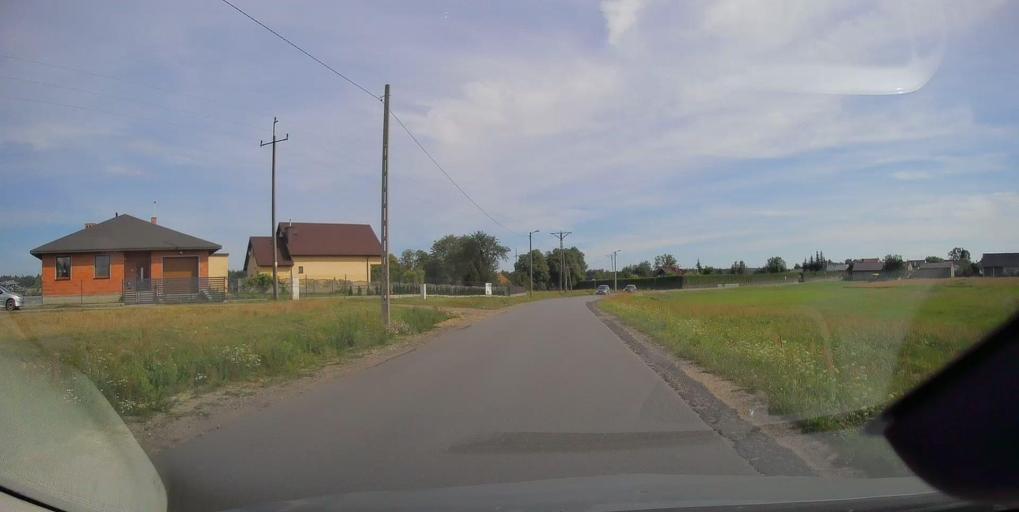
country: PL
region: Lodz Voivodeship
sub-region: Powiat tomaszowski
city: Tomaszow Mazowiecki
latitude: 51.4577
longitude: 20.0354
